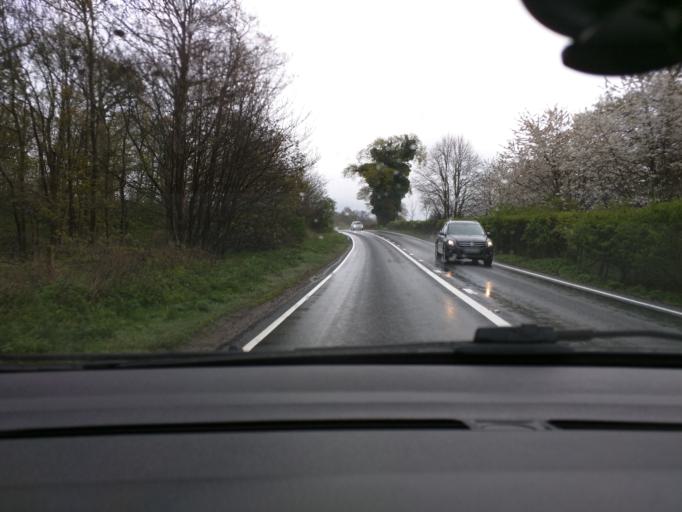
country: GB
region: England
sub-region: Suffolk
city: Saxmundham
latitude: 52.1845
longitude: 1.4327
